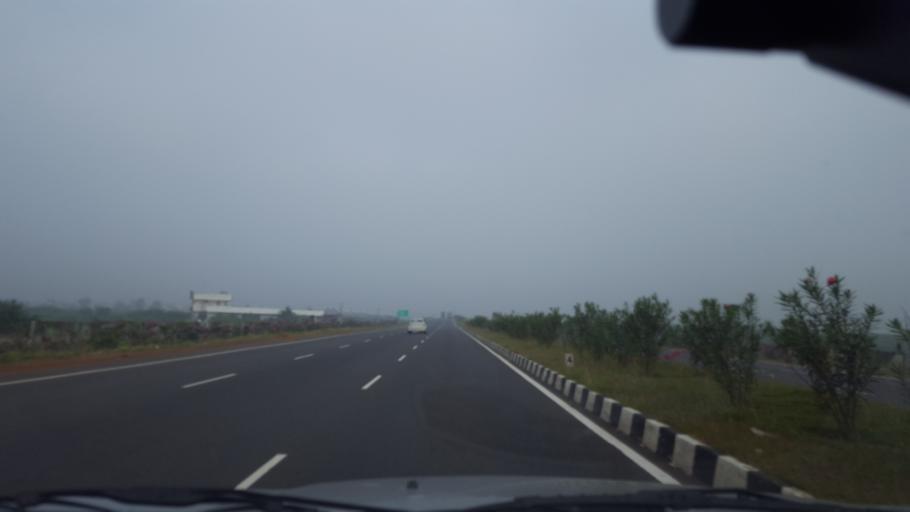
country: IN
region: Andhra Pradesh
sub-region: Prakasam
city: Ongole
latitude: 15.5252
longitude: 80.0604
